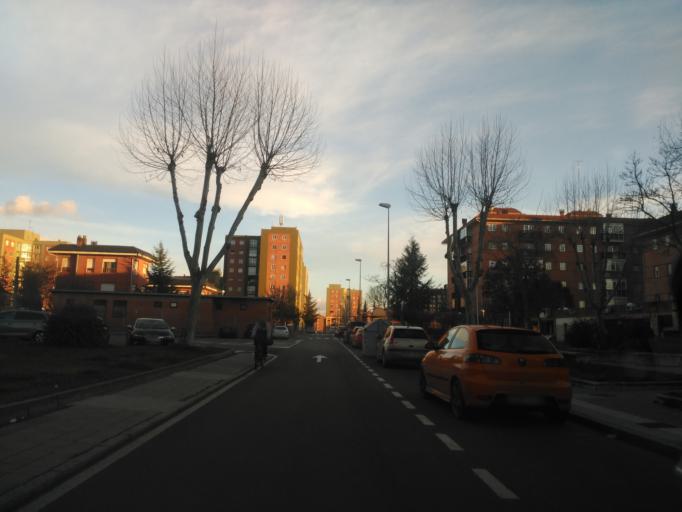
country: ES
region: Castille and Leon
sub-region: Provincia de Salamanca
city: Salamanca
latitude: 40.9518
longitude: -5.6647
